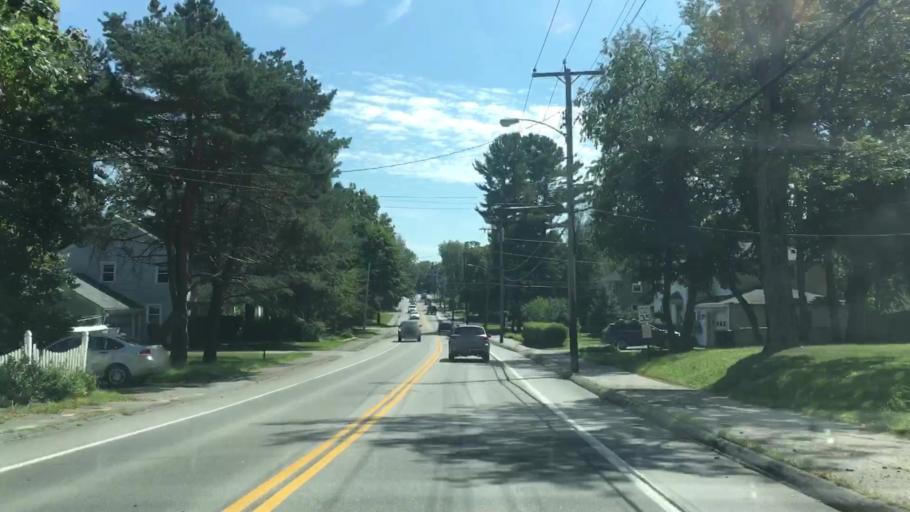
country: US
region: Maine
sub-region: Cumberland County
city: South Portland
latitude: 43.6282
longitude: -70.2509
